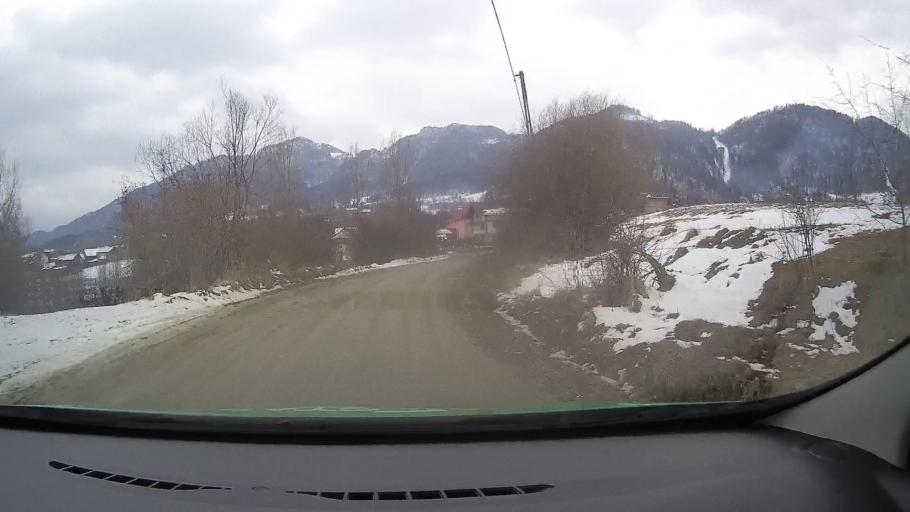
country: RO
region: Brasov
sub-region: Comuna Zarnesti
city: Zarnesti
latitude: 45.5456
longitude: 25.3224
